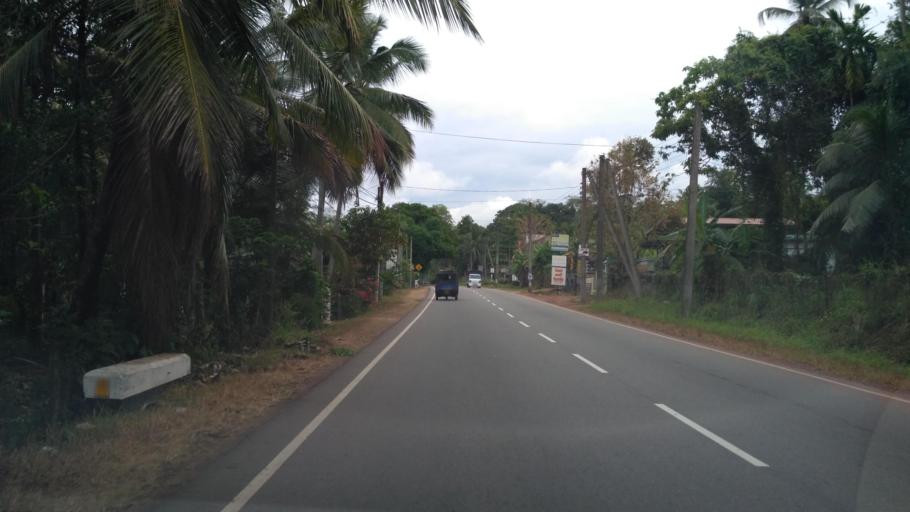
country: LK
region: North Western
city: Kuliyapitiya
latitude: 7.3272
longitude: 80.0521
